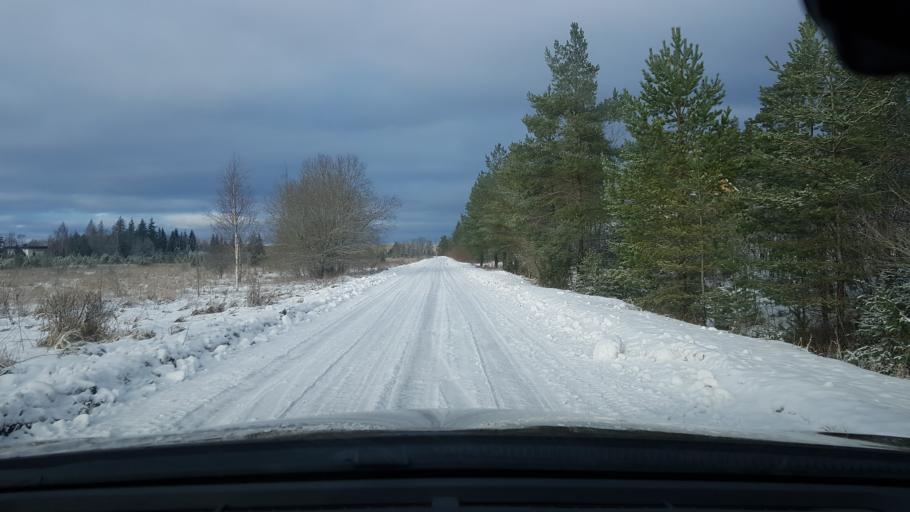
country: EE
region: Harju
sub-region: Keila linn
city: Keila
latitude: 59.3031
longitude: 24.2454
